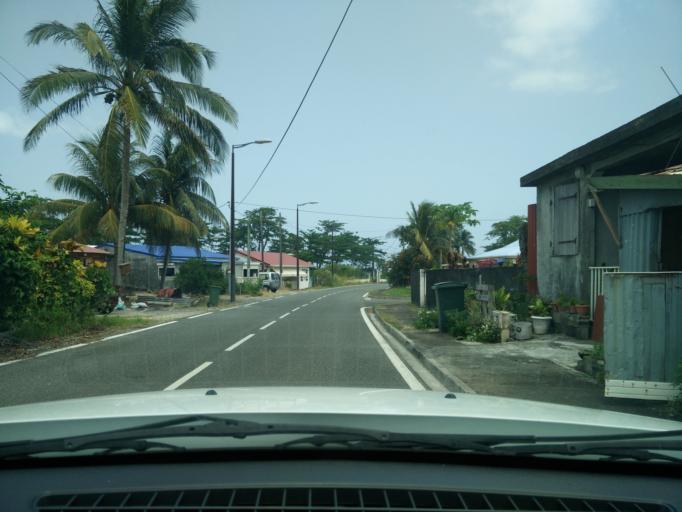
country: GP
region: Guadeloupe
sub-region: Guadeloupe
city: Capesterre-Belle-Eau
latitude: 16.0518
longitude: -61.5580
